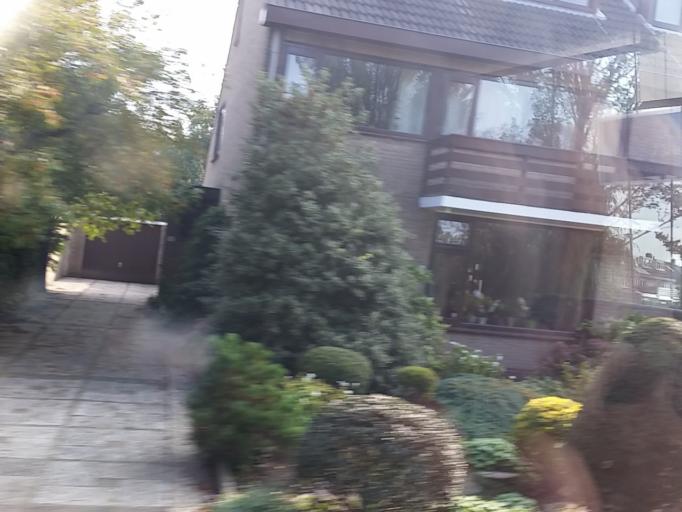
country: NL
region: South Holland
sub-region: Gemeente Noordwijk
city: Noordwijk-Binnen
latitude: 52.2441
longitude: 4.4509
